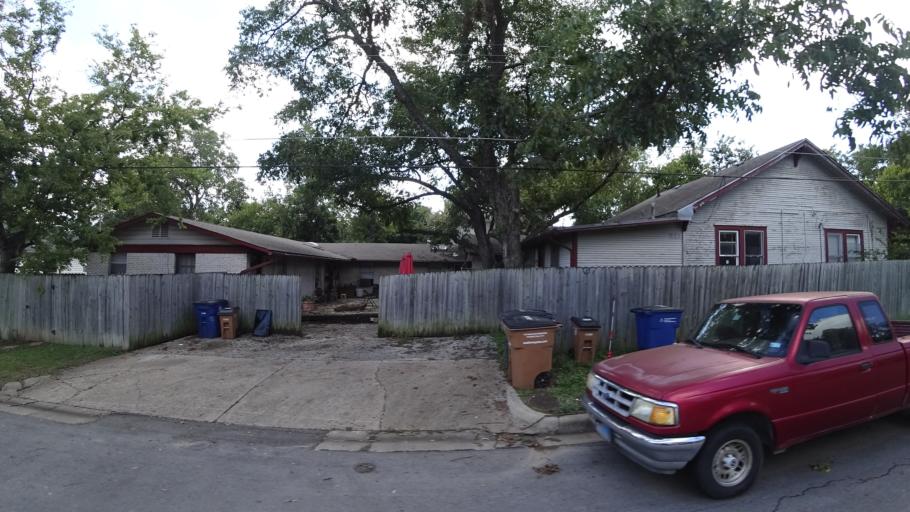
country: US
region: Texas
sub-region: Travis County
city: Austin
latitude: 30.3071
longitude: -97.7166
